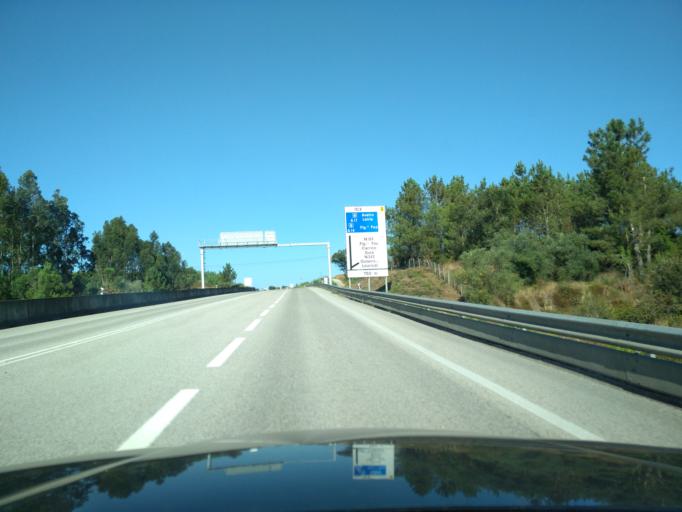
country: PT
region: Leiria
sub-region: Pombal
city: Lourical
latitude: 39.9886
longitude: -8.7762
